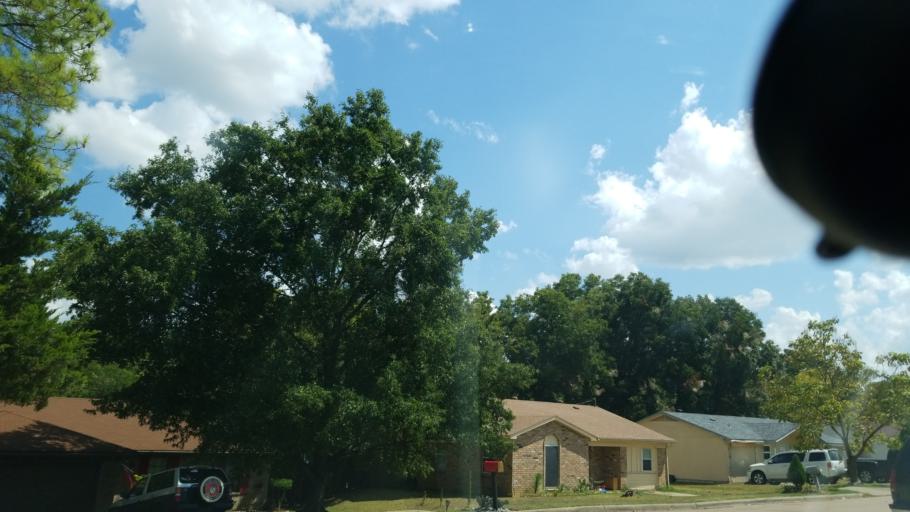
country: US
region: Texas
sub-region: Dallas County
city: Grand Prairie
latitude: 32.7285
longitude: -96.9904
